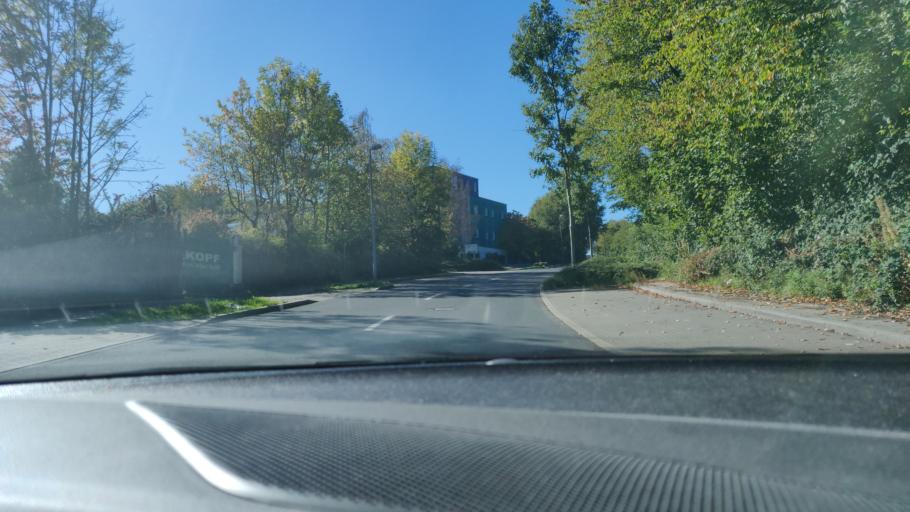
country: DE
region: North Rhine-Westphalia
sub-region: Regierungsbezirk Dusseldorf
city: Velbert
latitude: 51.3529
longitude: 7.0677
